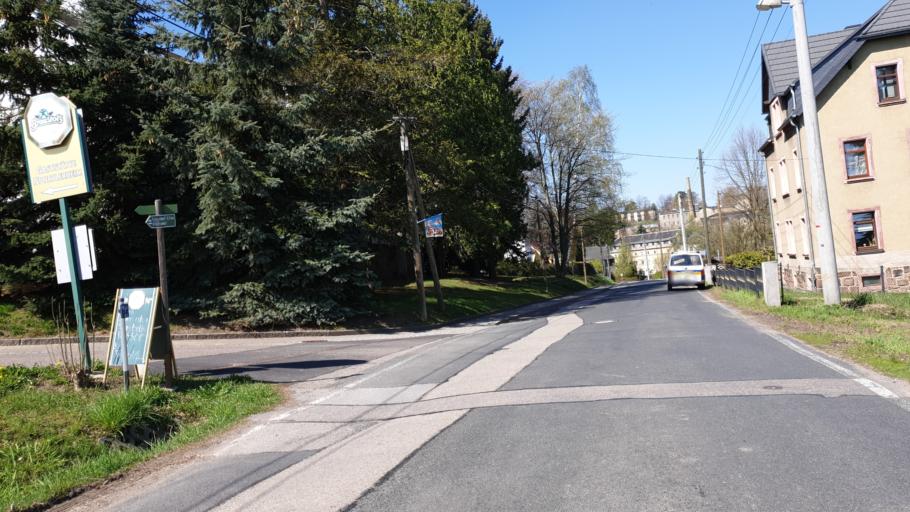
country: DE
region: Saxony
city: Taura
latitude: 50.9177
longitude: 12.8437
